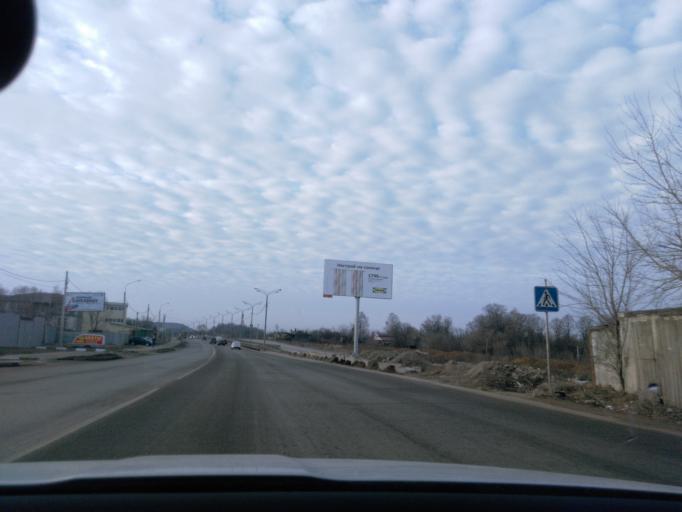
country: RU
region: Moskovskaya
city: Dolgoprudnyy
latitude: 55.9261
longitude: 37.4929
